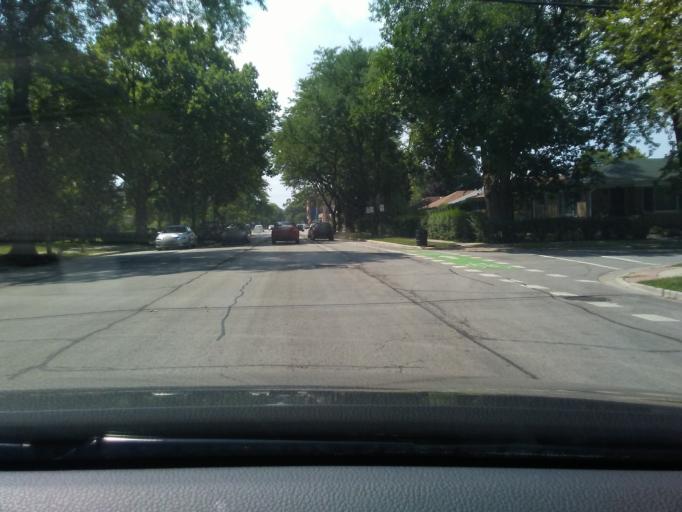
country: US
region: Illinois
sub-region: Cook County
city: Evanston
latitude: 42.0213
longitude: -87.6996
